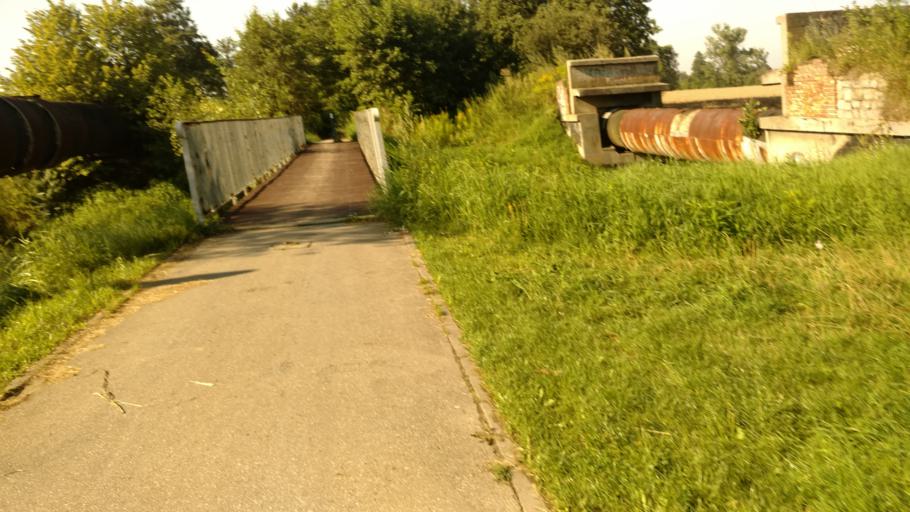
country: PL
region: Silesian Voivodeship
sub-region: Powiat pszczynski
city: Pszczyna
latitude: 49.9829
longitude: 18.9694
